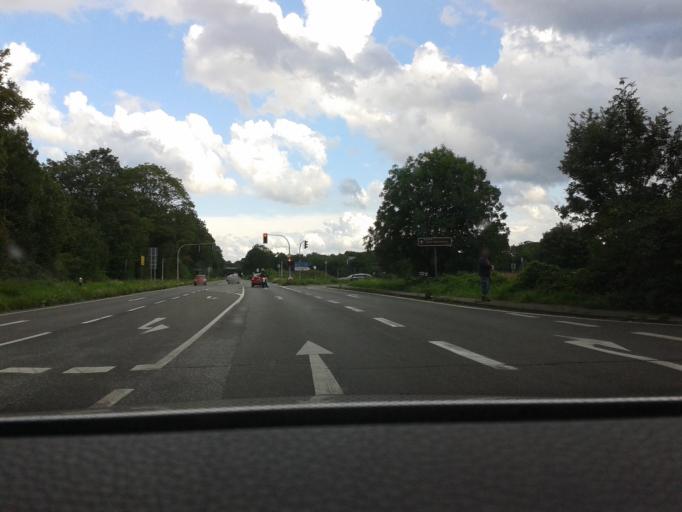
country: DE
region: North Rhine-Westphalia
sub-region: Regierungsbezirk Dusseldorf
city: Duisburg
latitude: 51.4444
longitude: 6.8117
